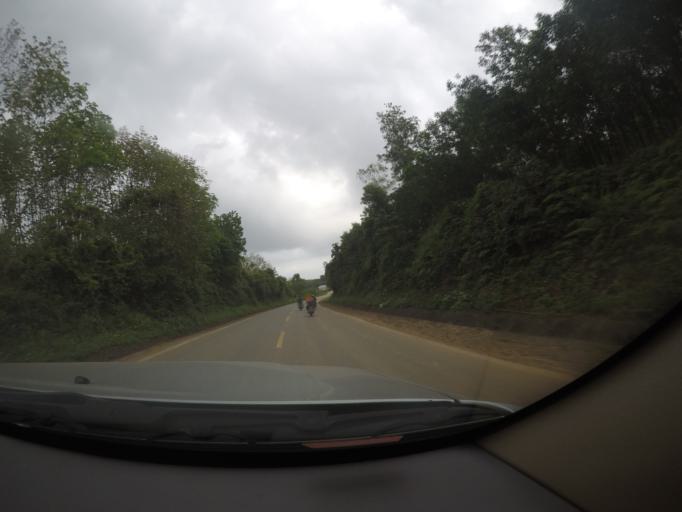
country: VN
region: Quang Tri
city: Ho Xa
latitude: 17.0364
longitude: 106.8946
